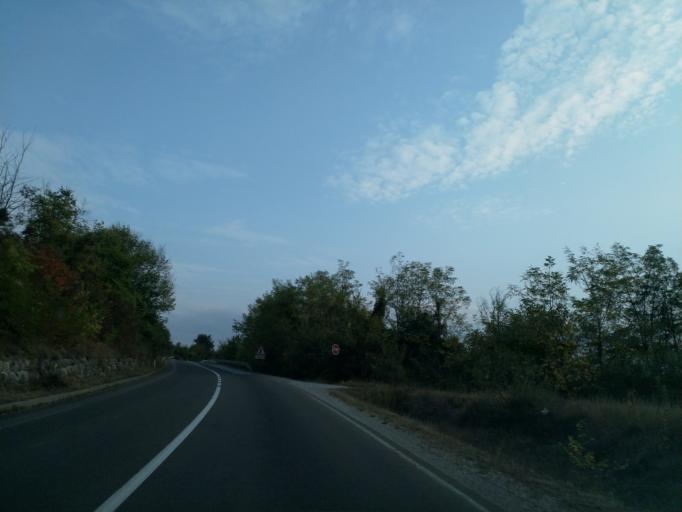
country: RS
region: Central Serbia
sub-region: Sumadijski Okrug
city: Topola
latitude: 44.2081
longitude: 20.7226
